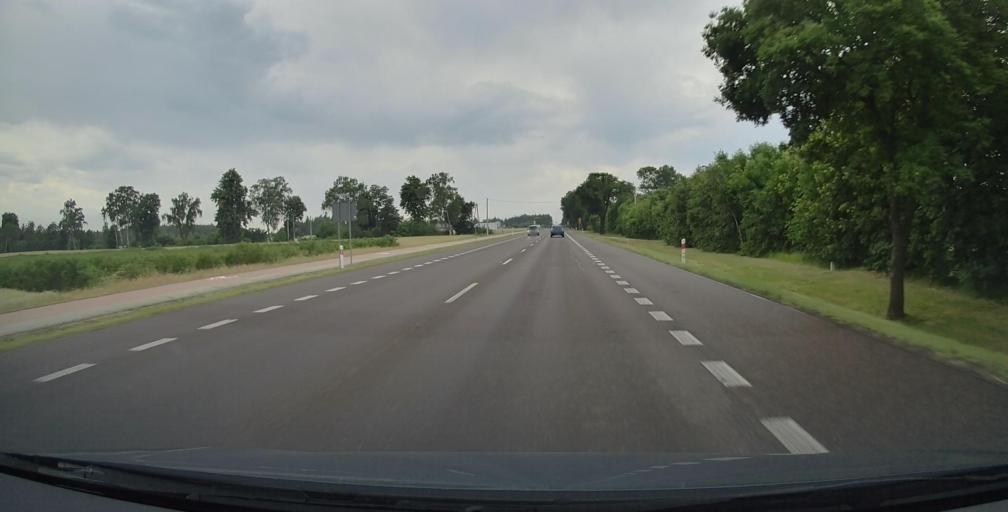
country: PL
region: Lublin Voivodeship
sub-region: Powiat bialski
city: Lesna Podlaska
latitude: 52.0358
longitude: 23.0139
